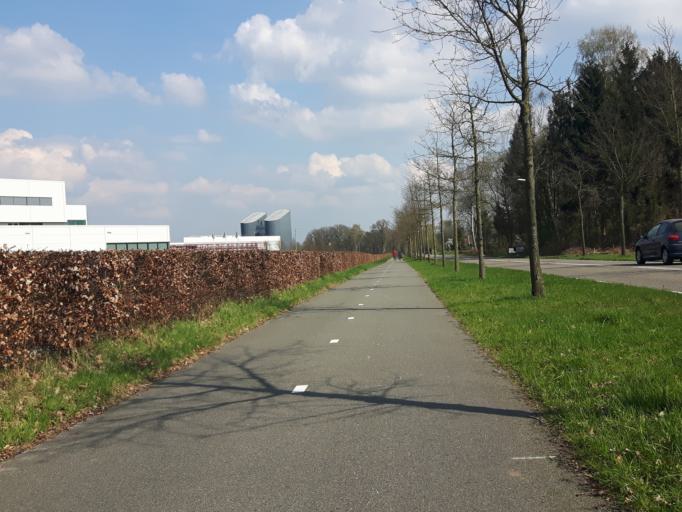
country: NL
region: Overijssel
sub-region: Gemeente Hengelo
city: Hengelo
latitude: 52.2048
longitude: 6.8141
